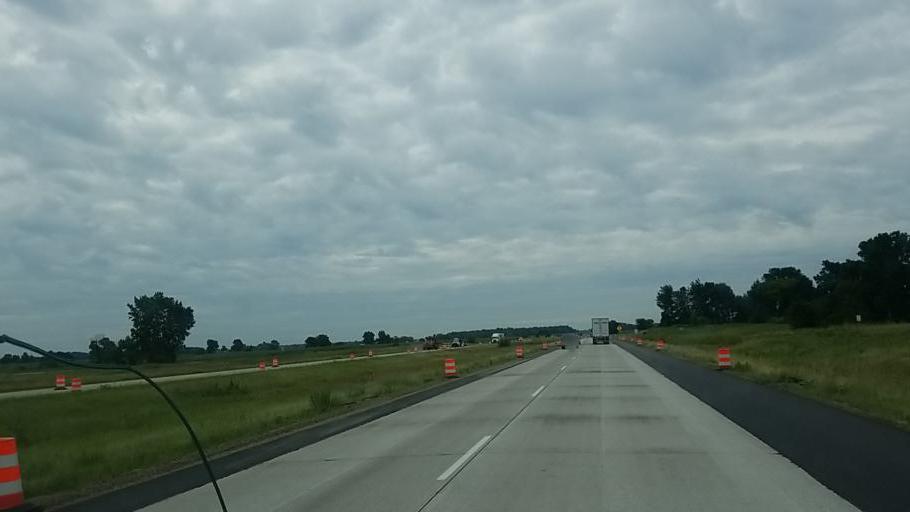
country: US
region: Indiana
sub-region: Steuben County
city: Fremont
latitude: 41.7957
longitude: -84.9951
